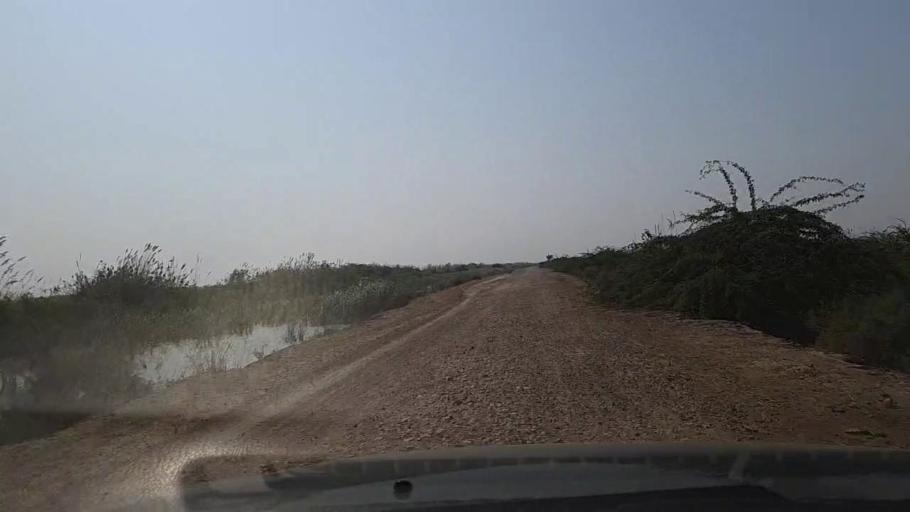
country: PK
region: Sindh
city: Mirpur Sakro
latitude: 24.3760
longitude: 67.6559
